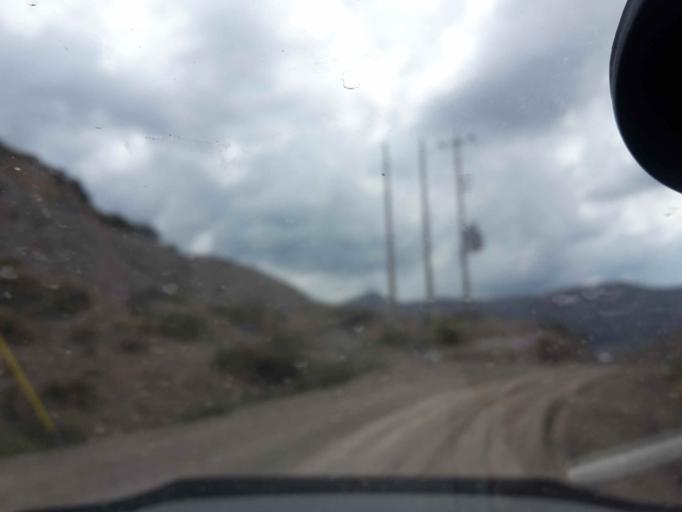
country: BO
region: Cochabamba
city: Colchani
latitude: -17.5152
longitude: -66.6042
